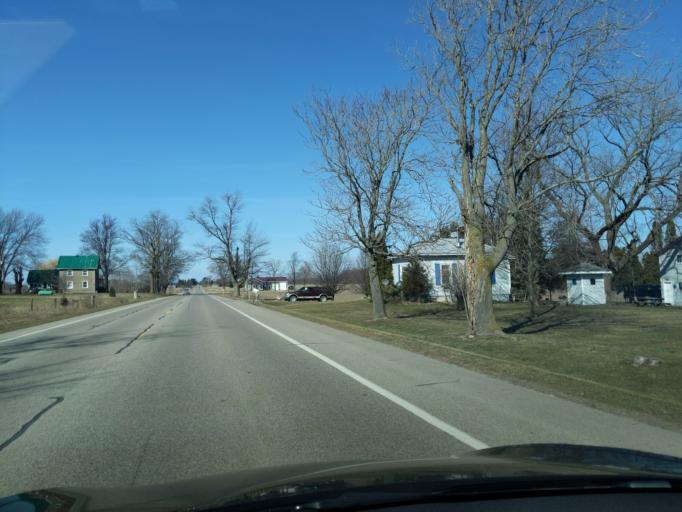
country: US
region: Michigan
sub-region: Ionia County
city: Lake Odessa
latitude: 42.8117
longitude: -85.1336
